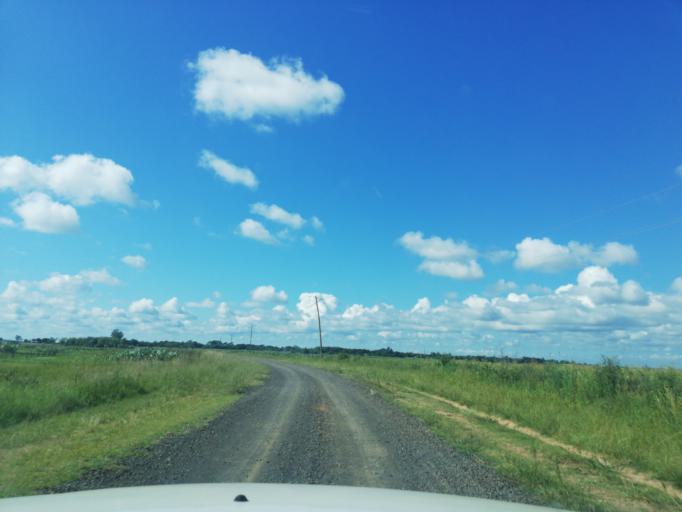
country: AR
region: Corrientes
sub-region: Departamento de San Miguel
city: San Miguel
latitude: -27.9741
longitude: -57.5803
